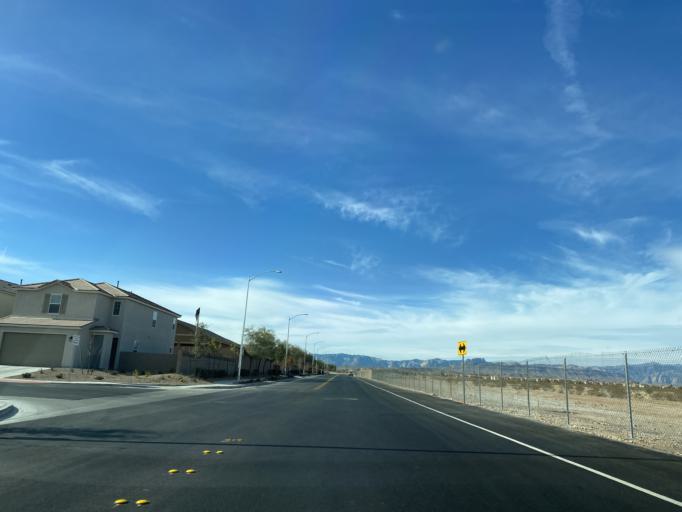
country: US
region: Nevada
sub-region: Clark County
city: Enterprise
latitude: 36.0423
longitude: -115.2127
